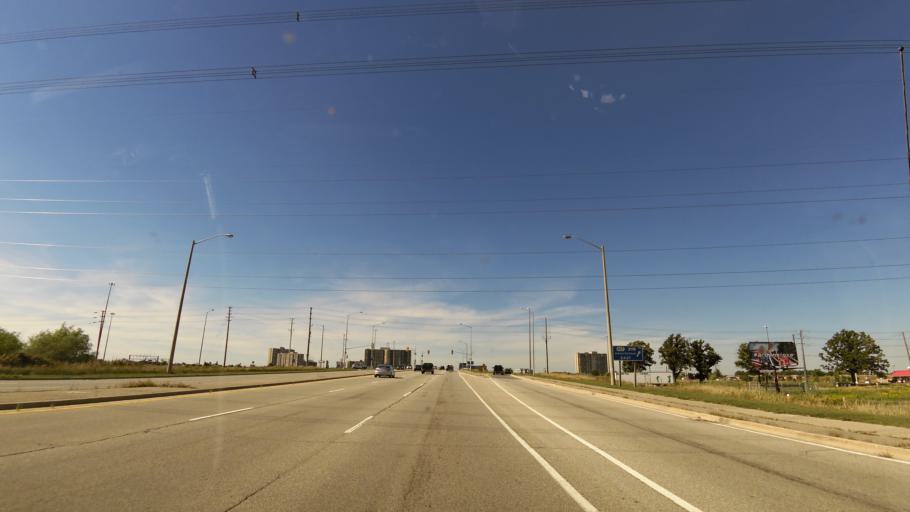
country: CA
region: Ontario
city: Brampton
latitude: 43.6517
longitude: -79.7136
